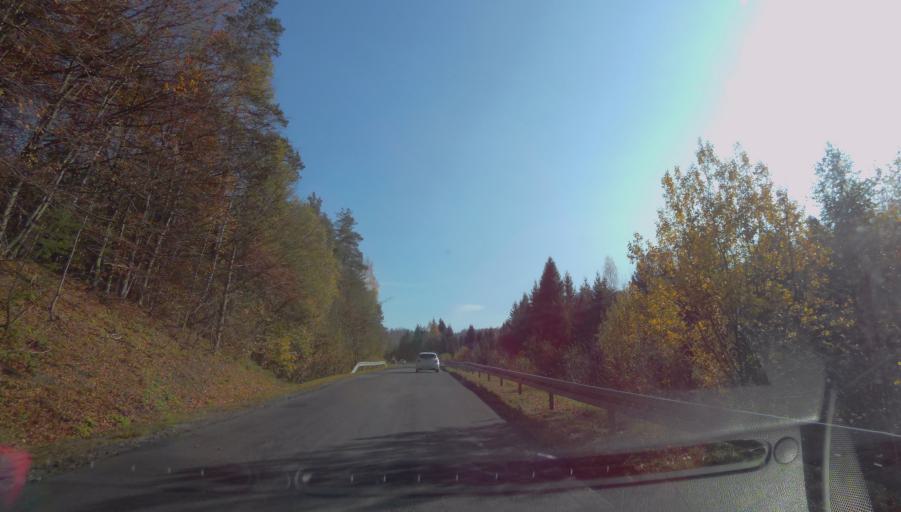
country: PL
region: Subcarpathian Voivodeship
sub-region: Powiat leski
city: Cisna
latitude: 49.2177
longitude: 22.2256
